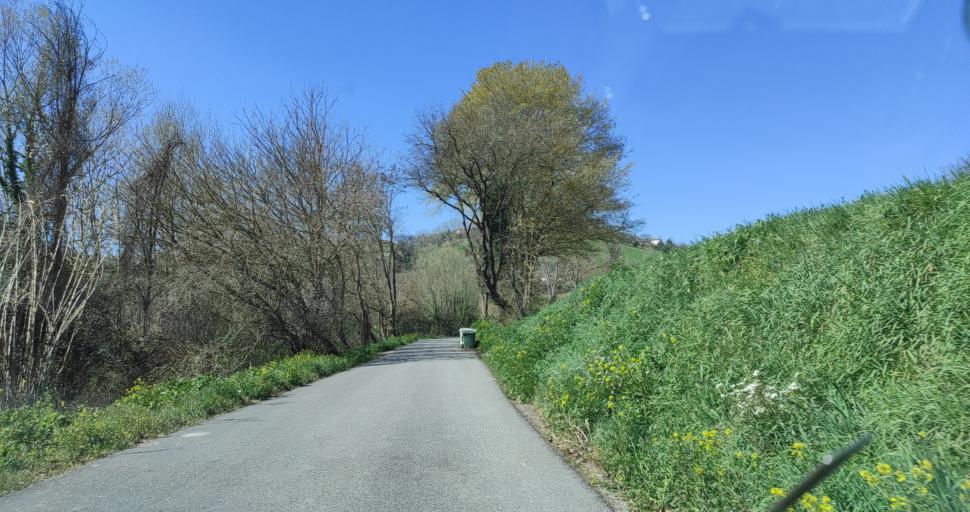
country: IT
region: The Marches
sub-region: Provincia di Macerata
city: Macerata
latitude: 43.3113
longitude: 13.4771
